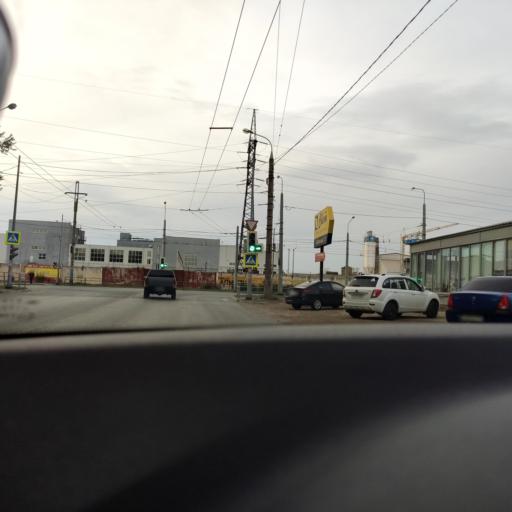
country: RU
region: Samara
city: Samara
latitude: 53.2018
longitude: 50.2648
